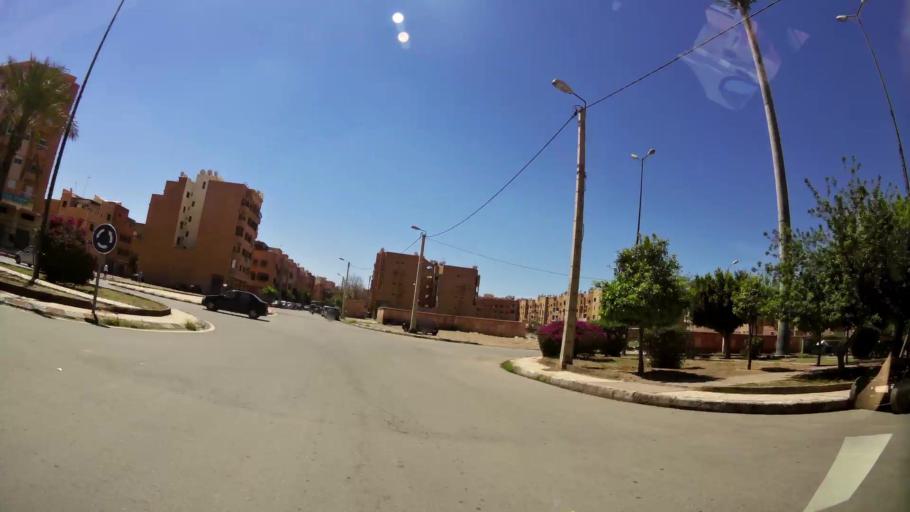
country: MA
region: Marrakech-Tensift-Al Haouz
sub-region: Marrakech
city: Marrakesh
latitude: 31.6343
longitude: -8.0626
